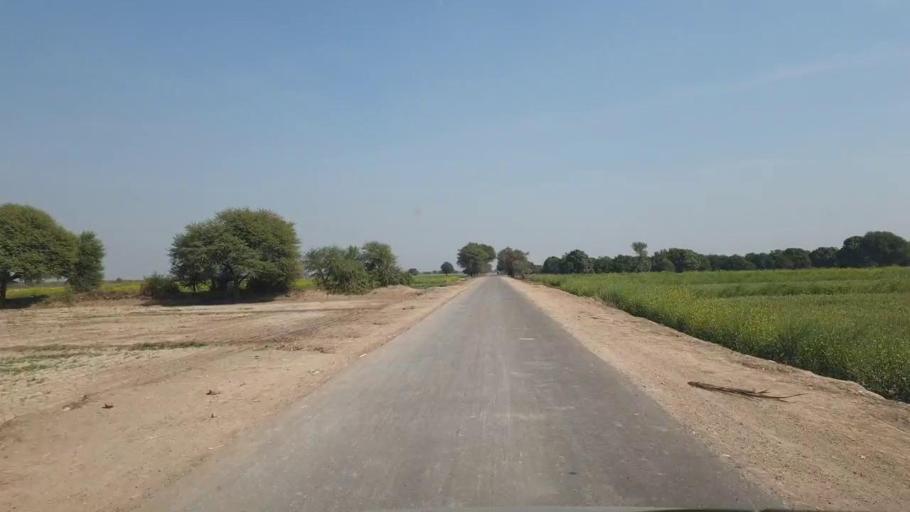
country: PK
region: Sindh
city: Chambar
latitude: 25.3116
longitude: 68.8069
